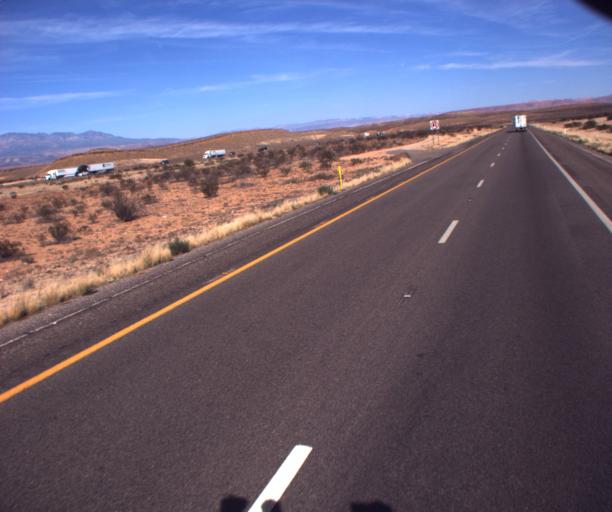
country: US
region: Utah
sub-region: Washington County
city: Saint George
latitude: 36.9856
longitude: -113.6348
